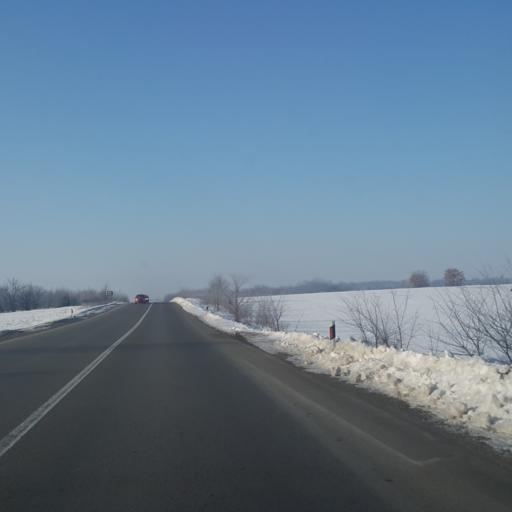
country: RS
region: Central Serbia
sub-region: Toplicki Okrug
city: Blace
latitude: 43.2402
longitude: 21.4197
